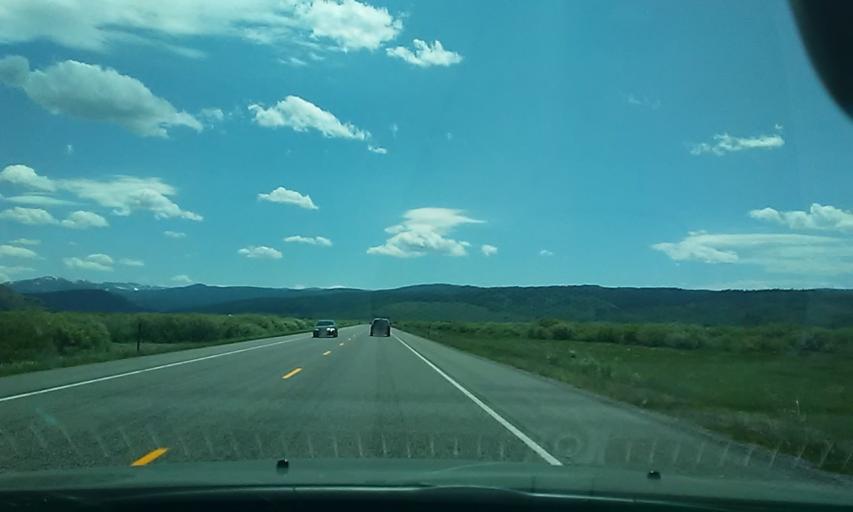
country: US
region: Wyoming
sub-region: Teton County
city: Jackson
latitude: 43.8366
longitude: -110.4343
